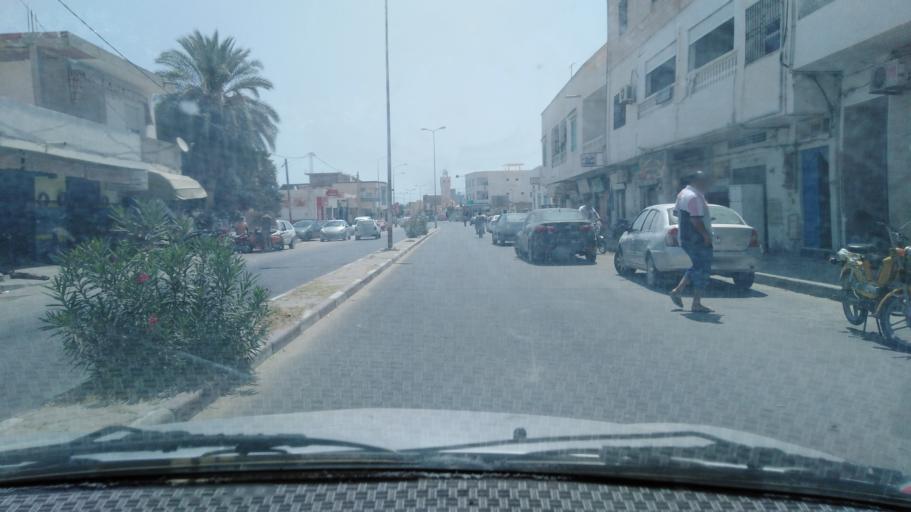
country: TN
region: Qabis
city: Gabes
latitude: 33.9594
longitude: 10.0005
